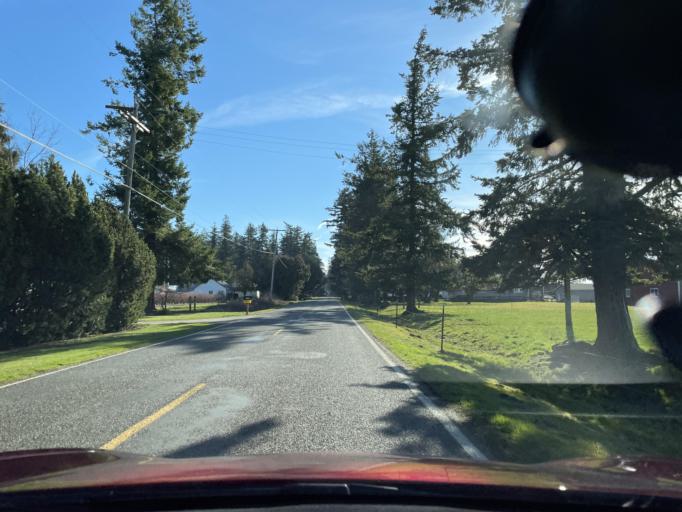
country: US
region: Washington
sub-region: Whatcom County
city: Lynden
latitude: 48.9742
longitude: -122.5130
